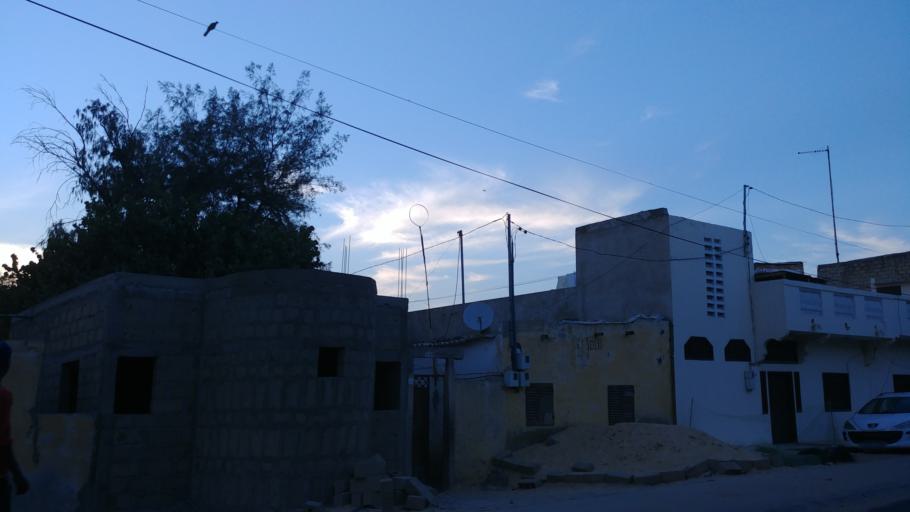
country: SN
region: Saint-Louis
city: Saint-Louis
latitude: 16.0151
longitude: -16.4895
